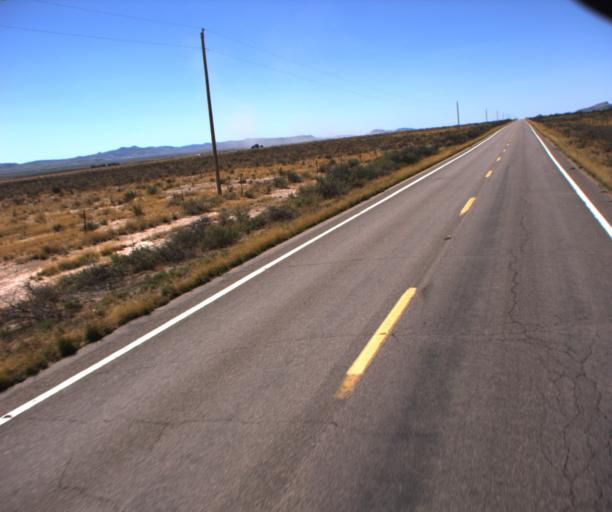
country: US
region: Arizona
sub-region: Cochise County
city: Douglas
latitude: 31.7785
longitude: -109.0717
